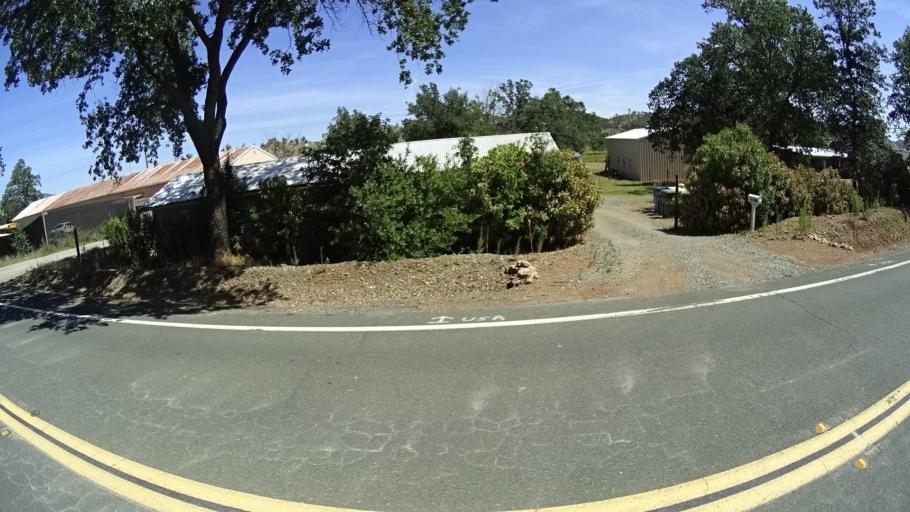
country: US
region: California
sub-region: Lake County
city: Middletown
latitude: 38.7502
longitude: -122.5945
